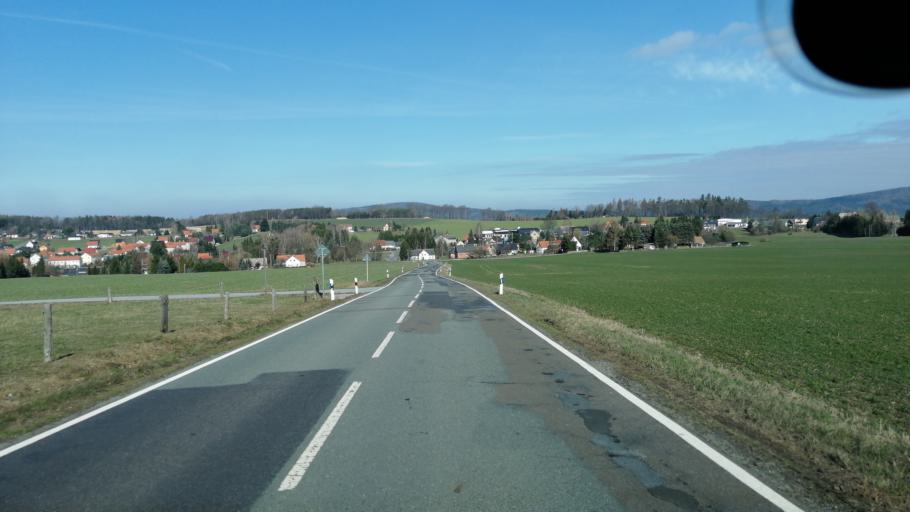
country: DE
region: Saxony
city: Beiersdorf
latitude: 51.0721
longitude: 14.5495
